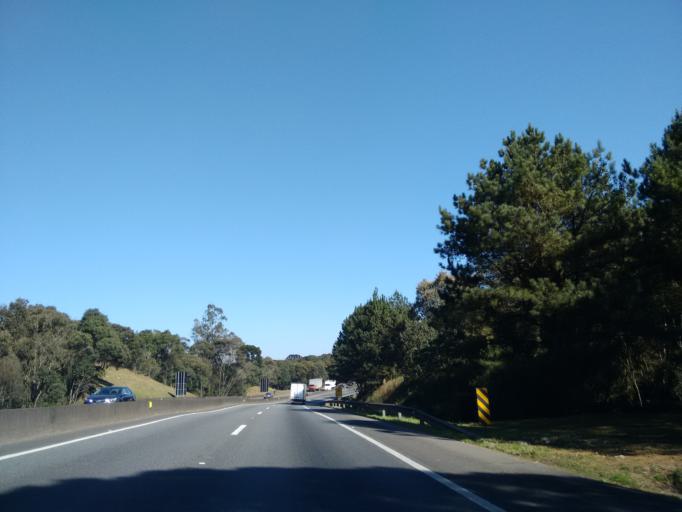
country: BR
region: Parana
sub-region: Sao Jose Dos Pinhais
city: Sao Jose dos Pinhais
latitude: -25.8462
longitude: -49.0920
